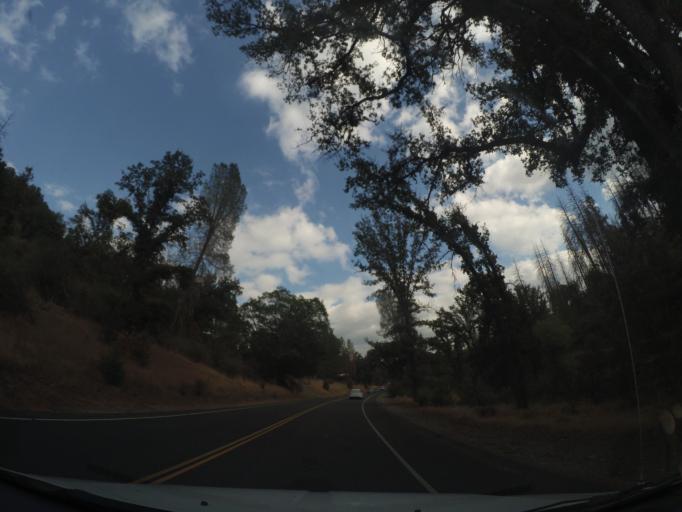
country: US
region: California
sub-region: Mariposa County
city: Midpines
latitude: 37.5554
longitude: -119.9283
